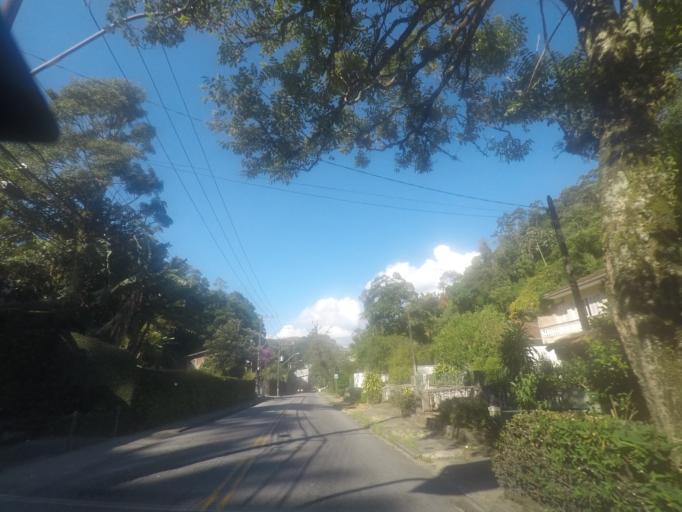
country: BR
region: Rio de Janeiro
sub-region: Petropolis
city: Petropolis
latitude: -22.5270
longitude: -43.1882
